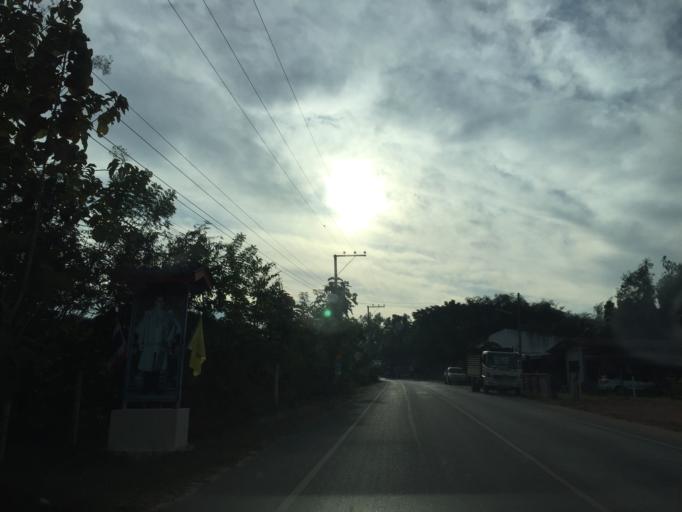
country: TH
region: Lamphun
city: Lamphun
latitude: 18.5120
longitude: 99.0269
